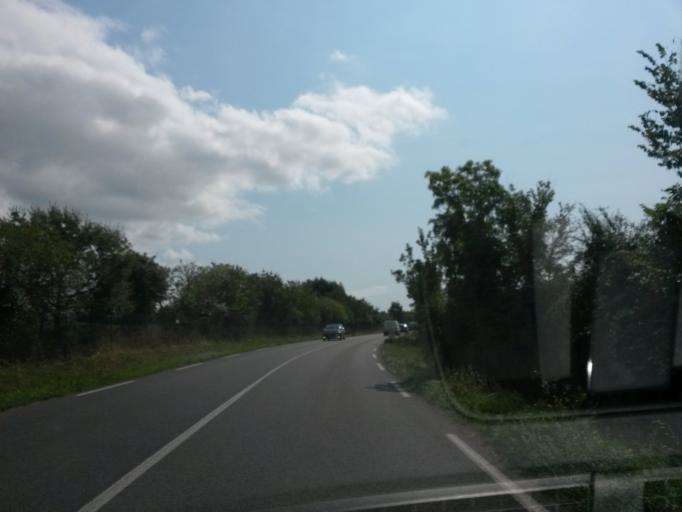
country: FR
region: Pays de la Loire
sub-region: Departement de la Vendee
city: Jard-sur-Mer
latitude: 46.4318
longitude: -1.5775
